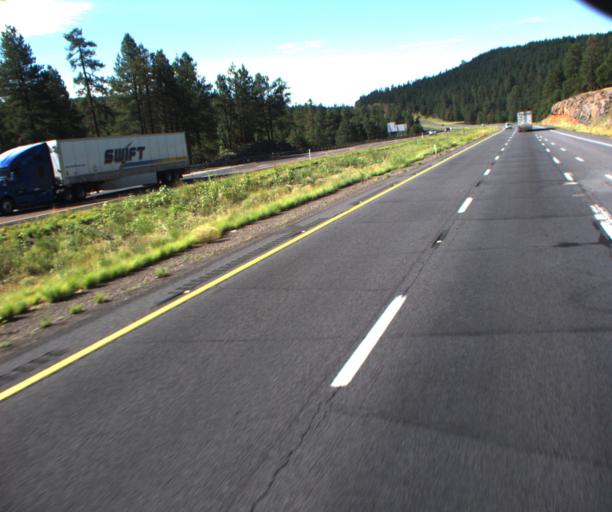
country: US
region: Arizona
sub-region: Coconino County
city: Mountainaire
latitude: 35.0476
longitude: -111.6842
